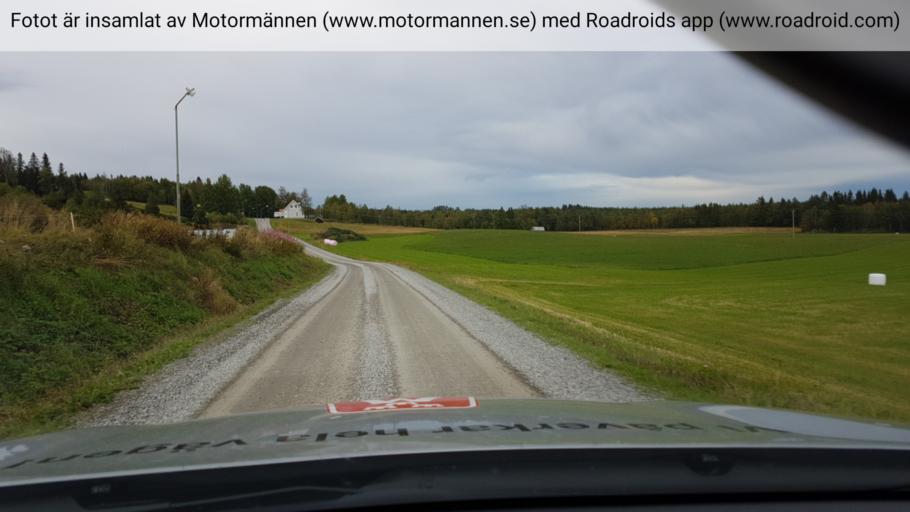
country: SE
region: Jaemtland
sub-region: Bergs Kommun
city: Hoverberg
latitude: 62.9411
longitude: 14.2717
